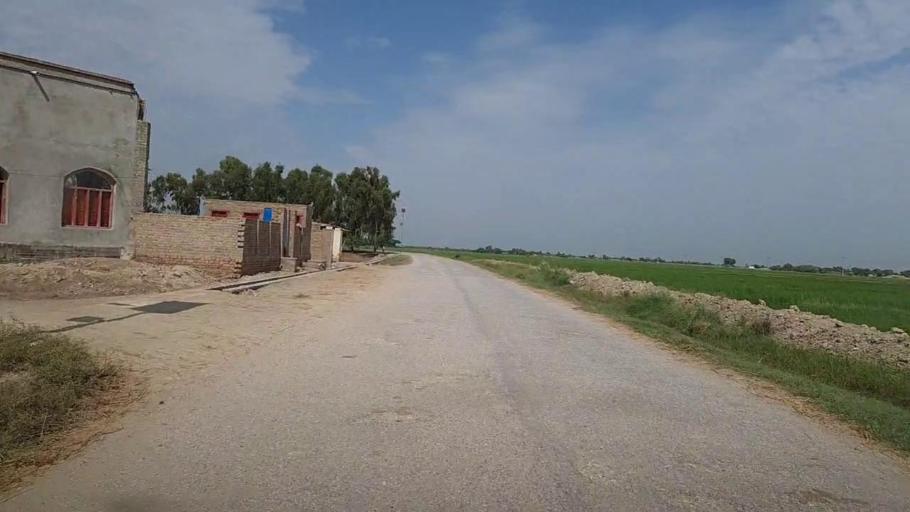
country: PK
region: Sindh
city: Thul
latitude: 28.2320
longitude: 68.7956
